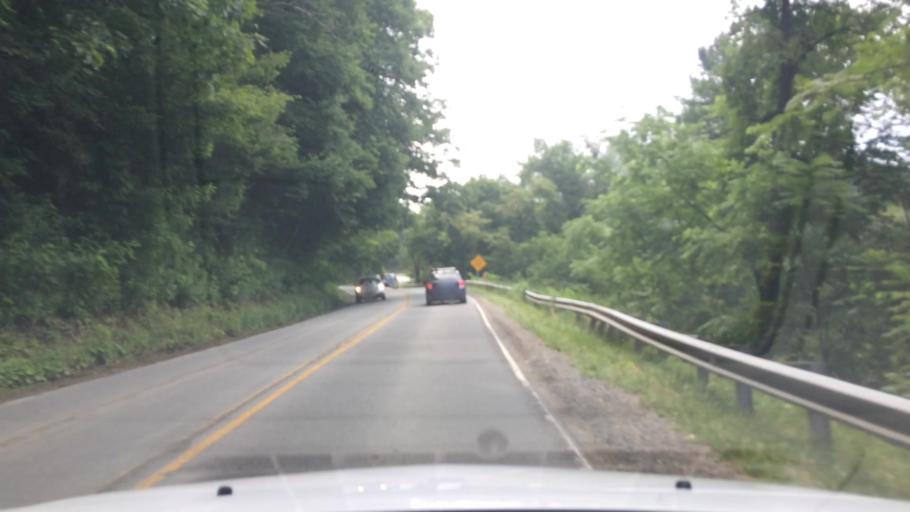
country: US
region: North Carolina
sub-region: Watauga County
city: Boone
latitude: 36.2187
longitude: -81.6379
